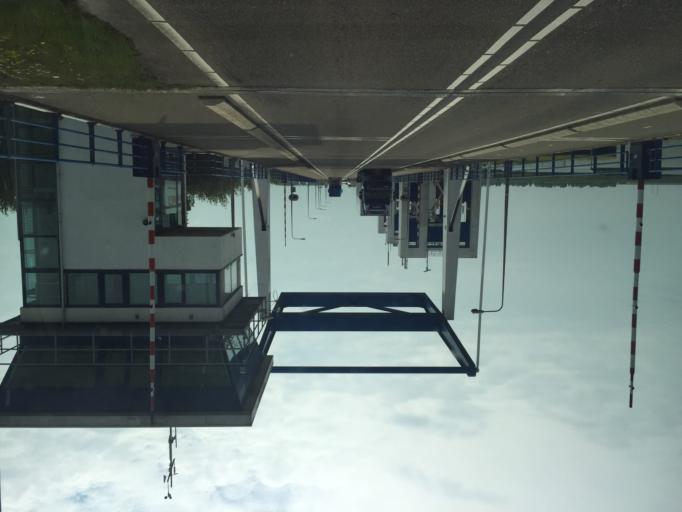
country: NL
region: North Holland
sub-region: Gemeente Enkhuizen
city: Enkhuizen
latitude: 52.6928
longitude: 5.2826
